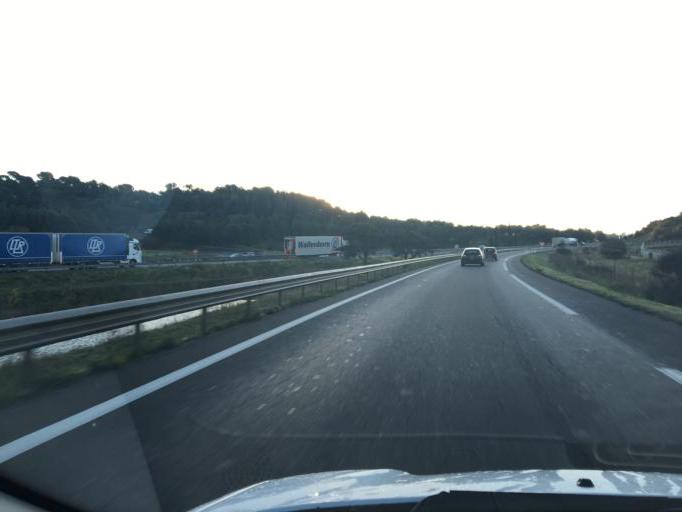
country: FR
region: Provence-Alpes-Cote d'Azur
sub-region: Departement du Vaucluse
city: Vedene
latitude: 43.9803
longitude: 4.8918
